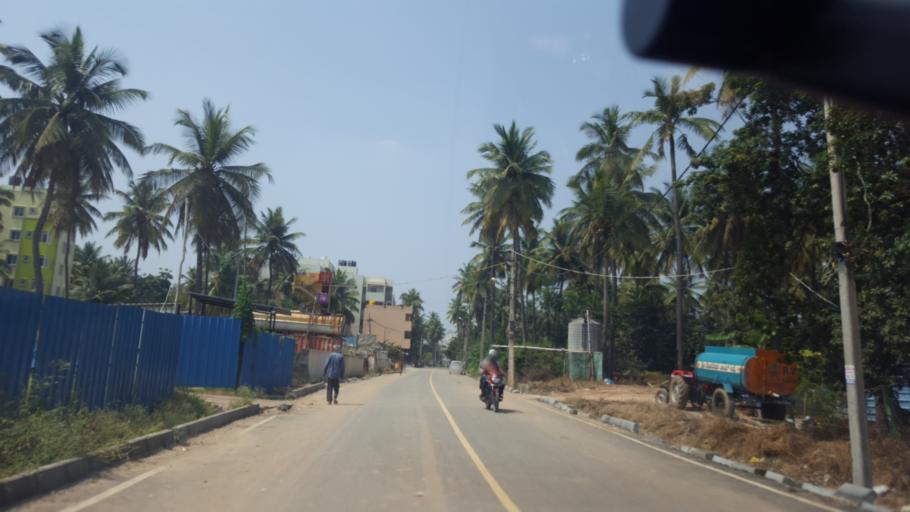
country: IN
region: Karnataka
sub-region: Bangalore Urban
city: Bangalore
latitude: 12.9399
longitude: 77.7063
